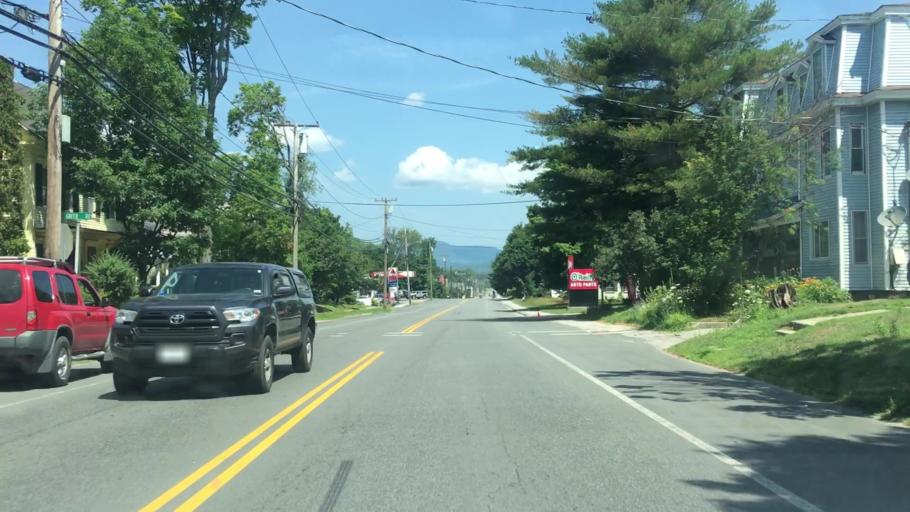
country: US
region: New Hampshire
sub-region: Sullivan County
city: Newport
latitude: 43.3701
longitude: -72.1774
